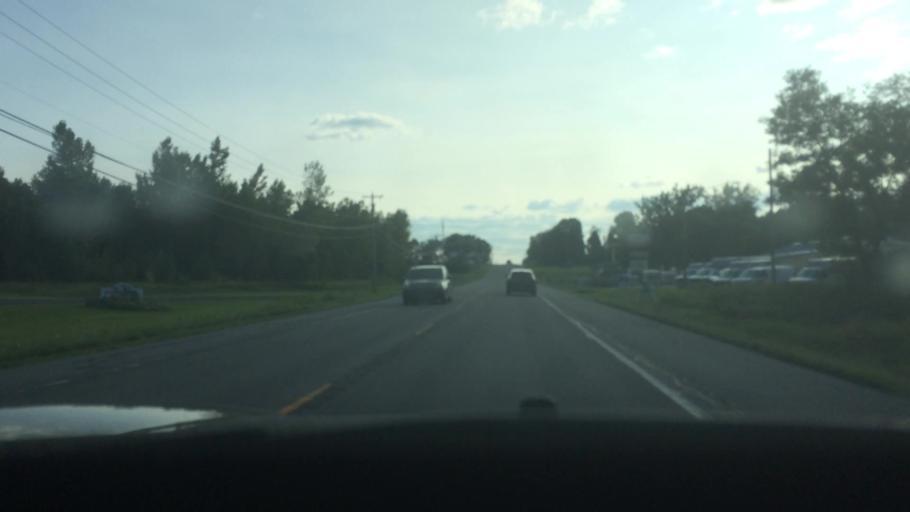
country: US
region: New York
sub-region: St. Lawrence County
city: Canton
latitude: 44.6101
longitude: -75.1212
